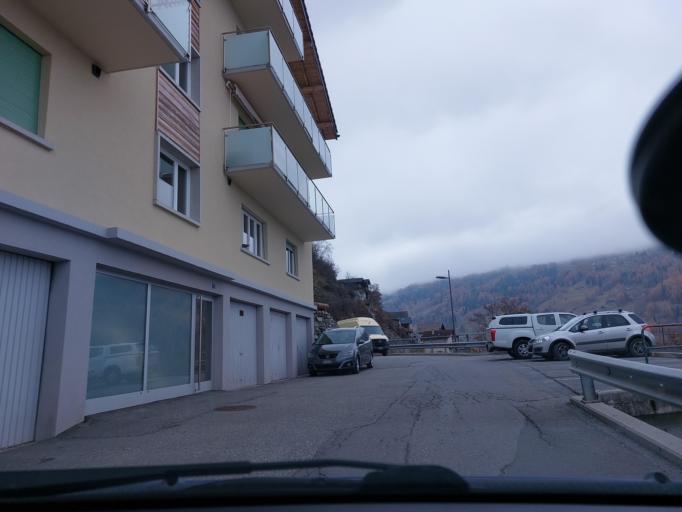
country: CH
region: Valais
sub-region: Martigny District
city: Riddes
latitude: 46.1663
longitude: 7.2440
